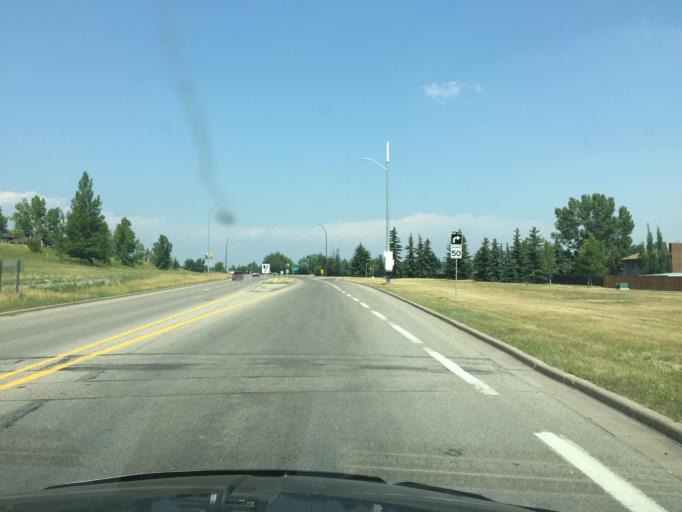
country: CA
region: Alberta
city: Calgary
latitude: 50.9155
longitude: -114.0164
